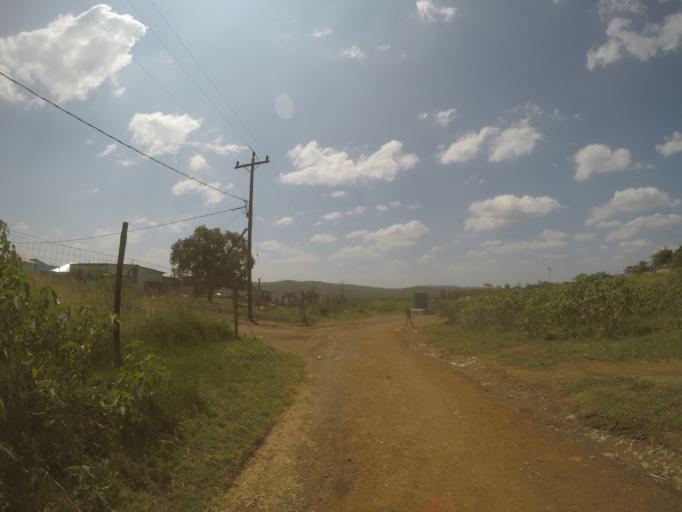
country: ZA
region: KwaZulu-Natal
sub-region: uThungulu District Municipality
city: Empangeni
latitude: -28.5911
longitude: 31.7398
